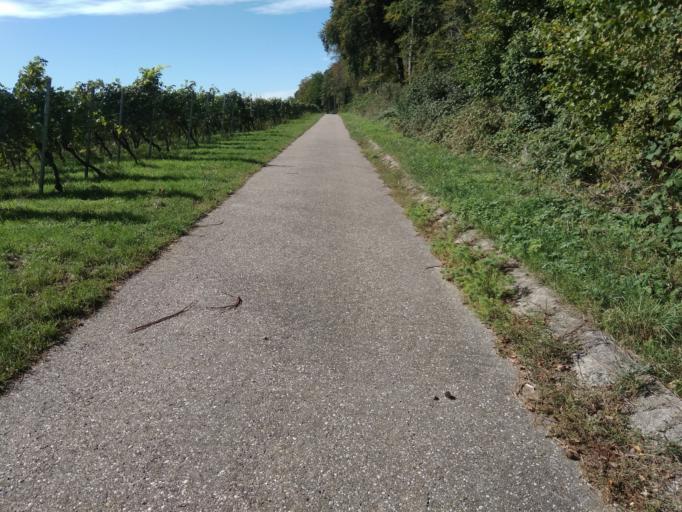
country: DE
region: Baden-Wuerttemberg
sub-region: Regierungsbezirk Stuttgart
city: Eberstadt
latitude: 49.1670
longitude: 9.3237
